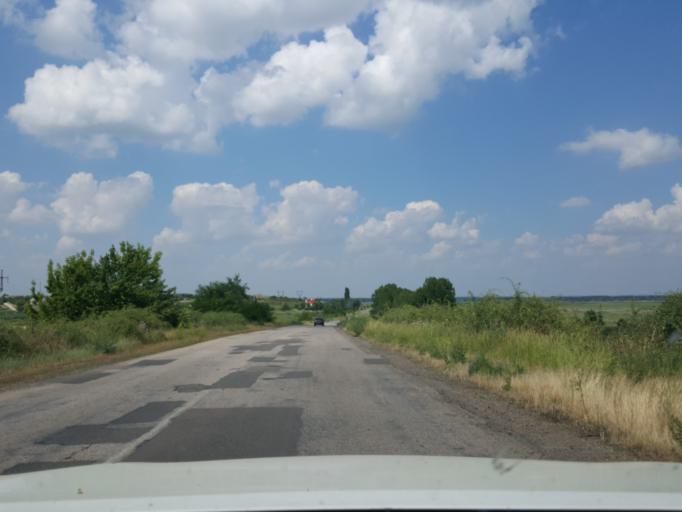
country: UA
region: Odessa
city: Starokozache
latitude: 46.3931
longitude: 30.0918
